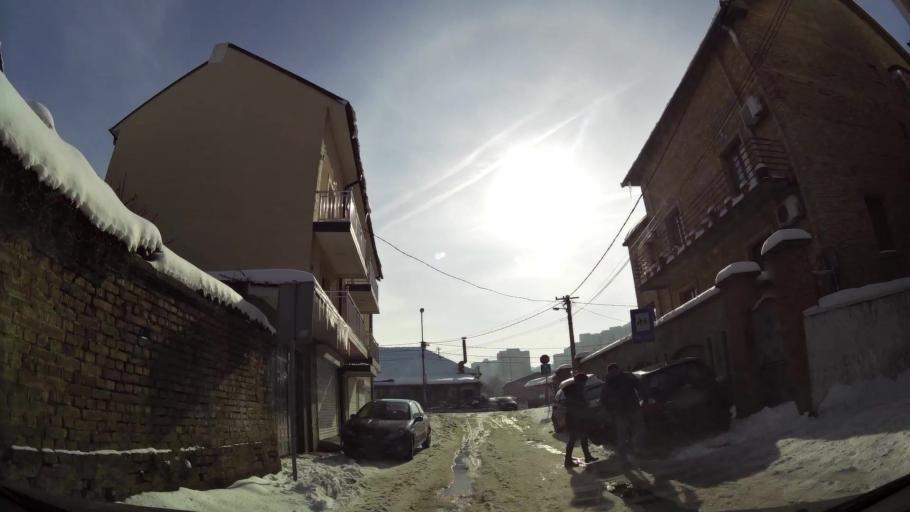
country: RS
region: Central Serbia
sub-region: Belgrade
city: Zvezdara
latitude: 44.7949
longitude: 20.5285
